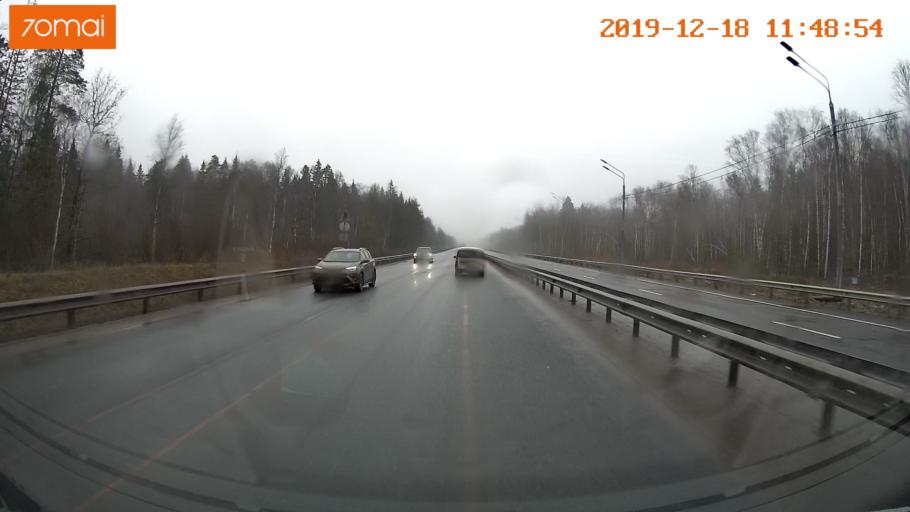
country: RU
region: Moskovskaya
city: Yershovo
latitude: 55.7726
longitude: 36.9074
